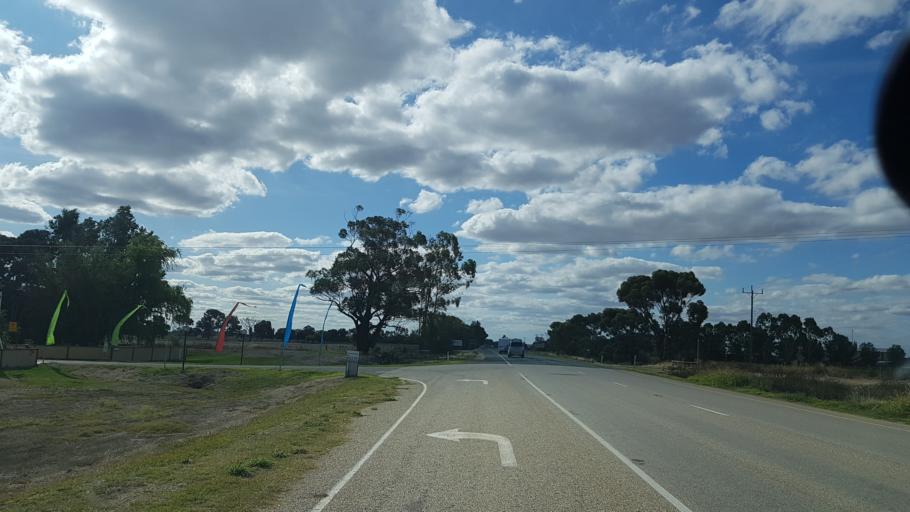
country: AU
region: Victoria
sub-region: Swan Hill
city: Swan Hill
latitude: -35.7605
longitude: 143.9298
